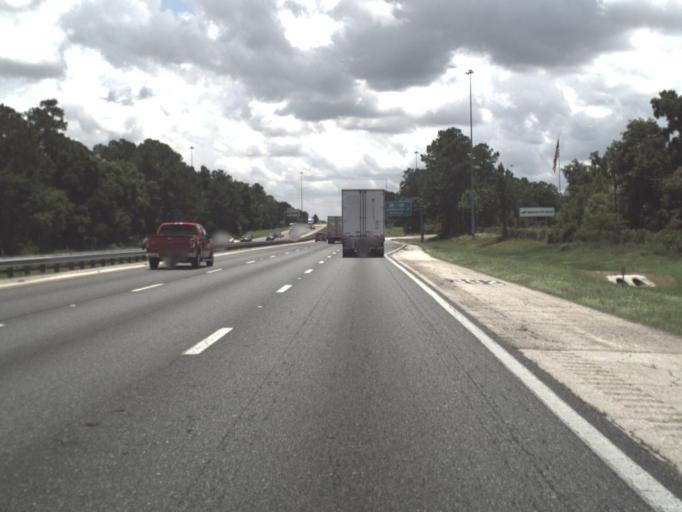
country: US
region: Florida
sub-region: Alachua County
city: Gainesville
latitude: 29.6061
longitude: -82.3771
